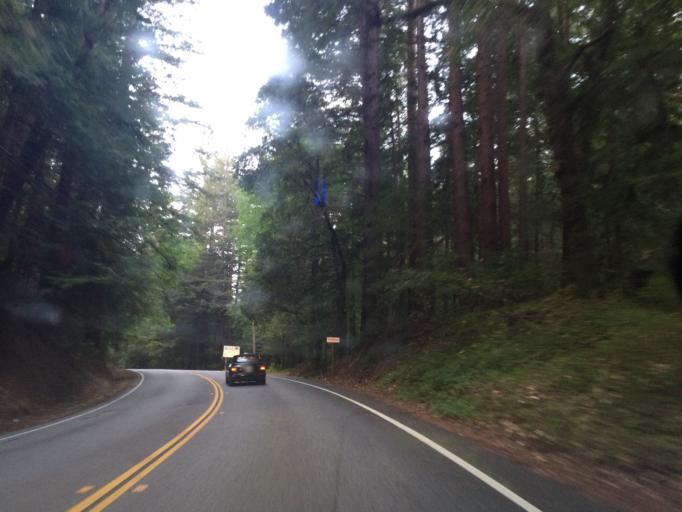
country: US
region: California
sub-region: Santa Cruz County
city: Boulder Creek
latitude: 37.2058
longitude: -122.1450
